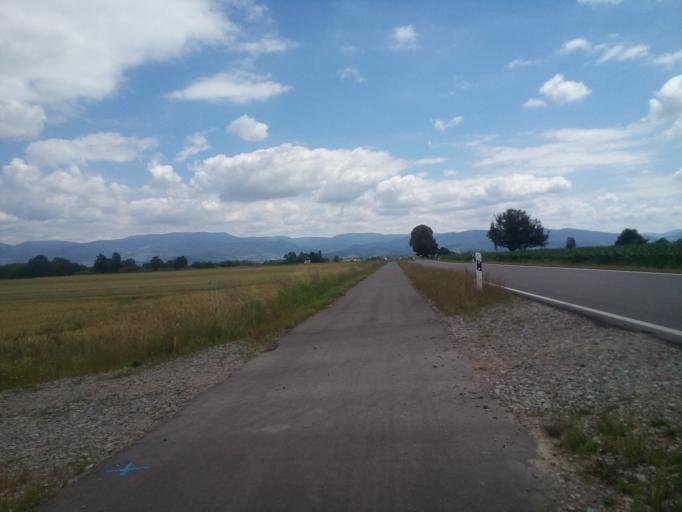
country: DE
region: Baden-Wuerttemberg
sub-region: Freiburg Region
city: Renchen
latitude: 48.6162
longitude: 7.9722
